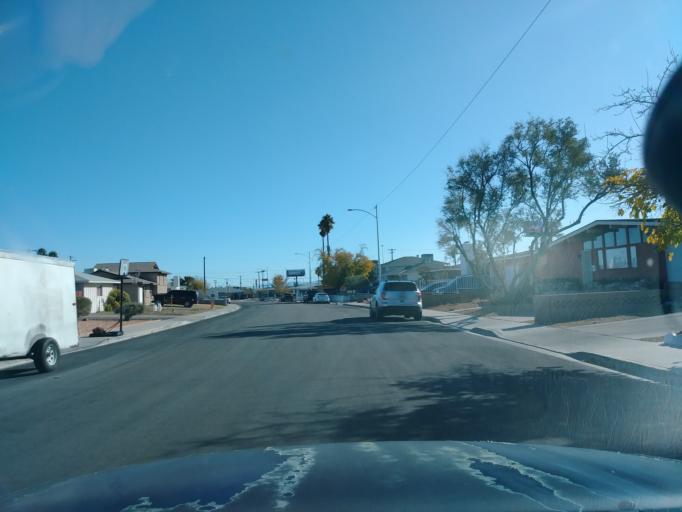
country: US
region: Nevada
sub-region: Clark County
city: Spring Valley
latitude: 36.1760
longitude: -115.2280
